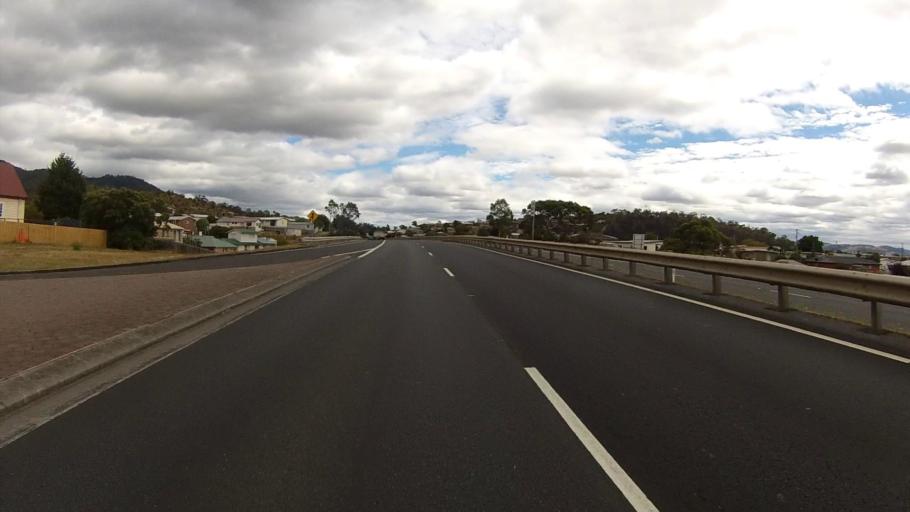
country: AU
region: Tasmania
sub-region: Glenorchy
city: Claremont
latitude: -42.7888
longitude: 147.2446
